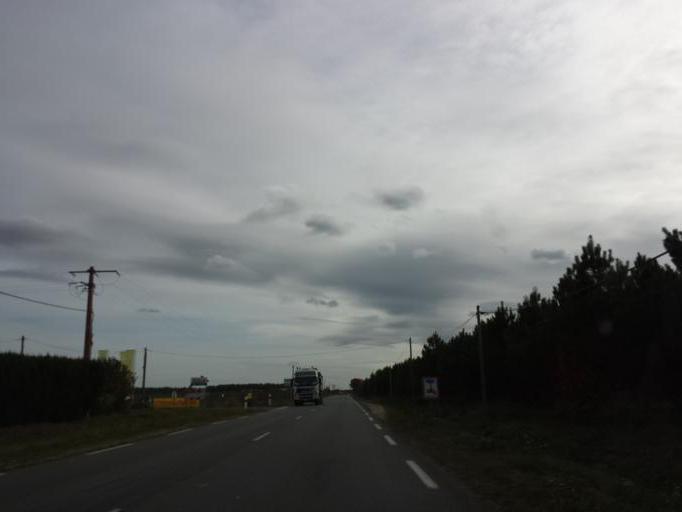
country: FR
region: Aquitaine
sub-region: Departement de la Gironde
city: Marcheprime
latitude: 44.7706
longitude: -0.9264
